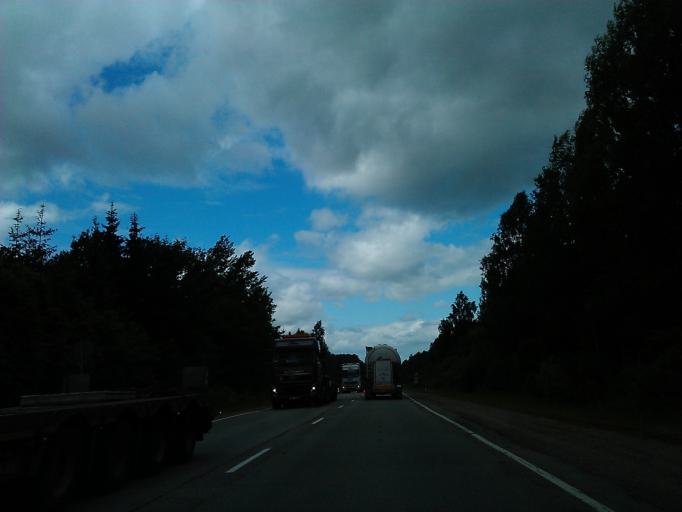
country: LV
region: Tukuma Rajons
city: Tukums
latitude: 56.9341
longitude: 23.1955
